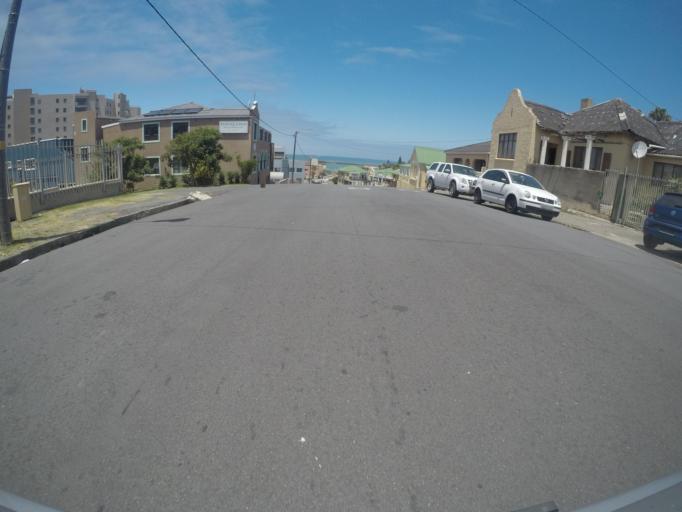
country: ZA
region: Eastern Cape
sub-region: Buffalo City Metropolitan Municipality
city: East London
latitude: -33.0179
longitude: 27.9168
